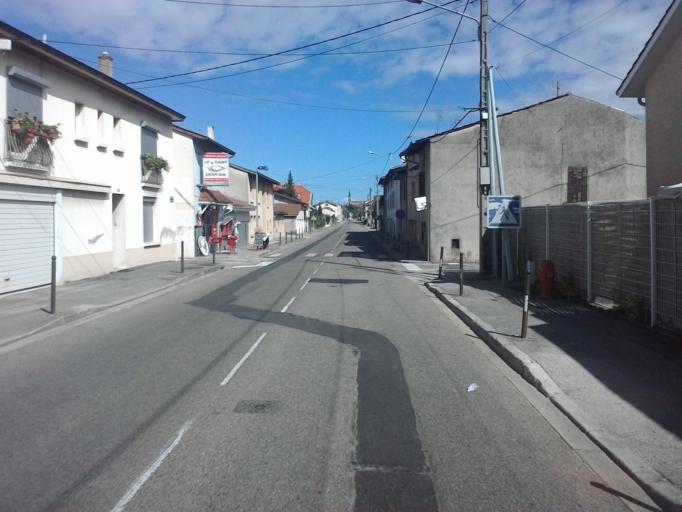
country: FR
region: Rhone-Alpes
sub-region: Departement de l'Ain
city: Vaux-en-Bugey
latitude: 45.9486
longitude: 5.3668
